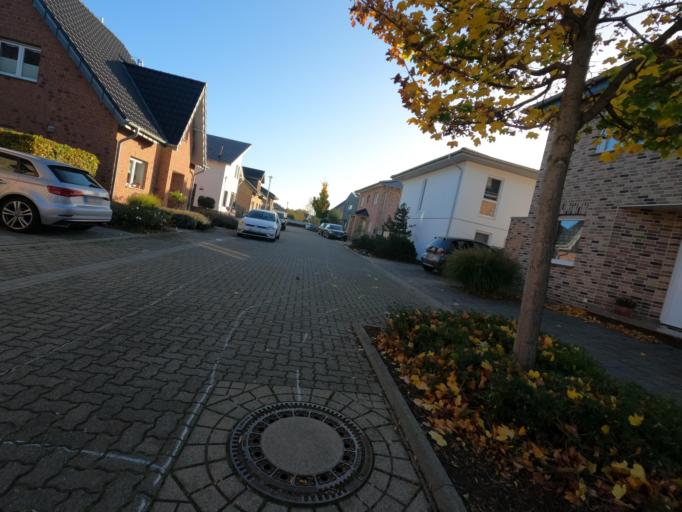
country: DE
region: North Rhine-Westphalia
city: Erkelenz
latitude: 51.0827
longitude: 6.2945
